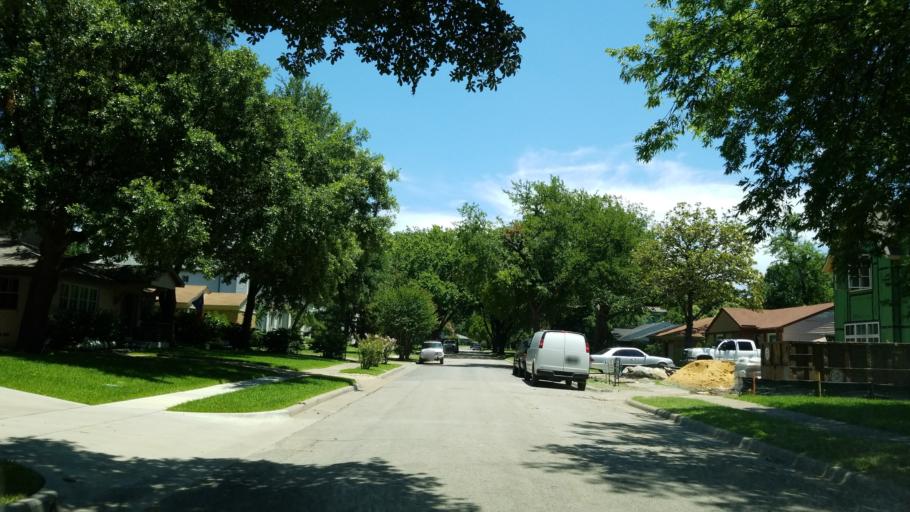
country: US
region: Texas
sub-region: Dallas County
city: University Park
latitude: 32.8725
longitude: -96.8491
